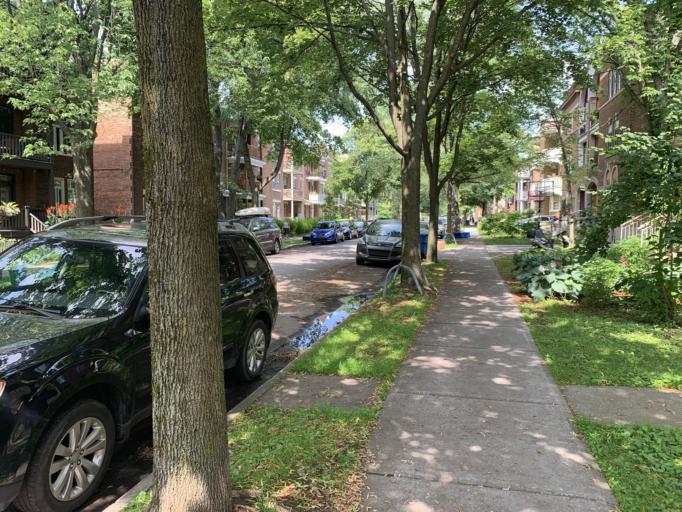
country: CA
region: Quebec
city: Quebec
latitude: 46.8004
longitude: -71.2316
